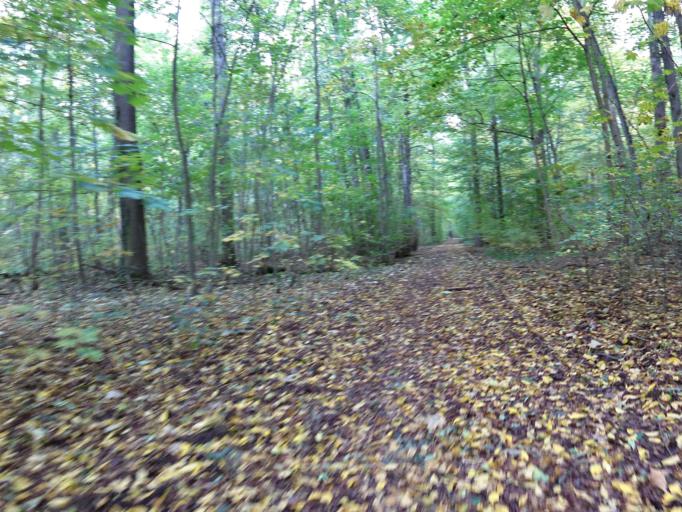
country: DE
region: Saxony
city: Markkleeberg
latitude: 51.3056
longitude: 12.3501
